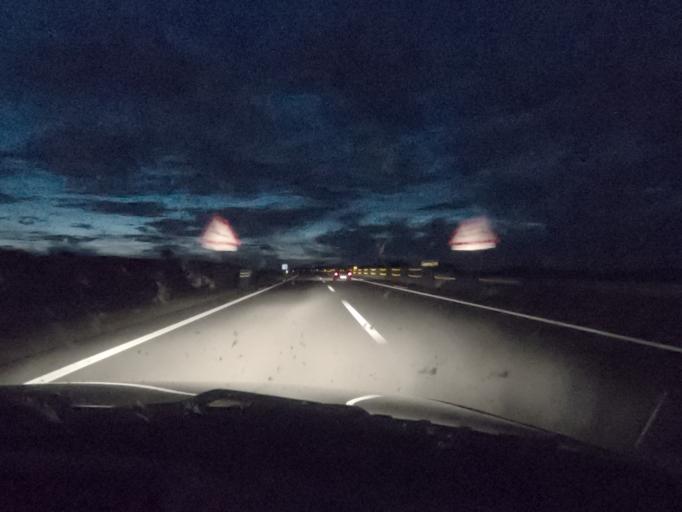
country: ES
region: Extremadura
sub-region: Provincia de Caceres
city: Morcillo
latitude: 39.9864
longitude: -6.4286
